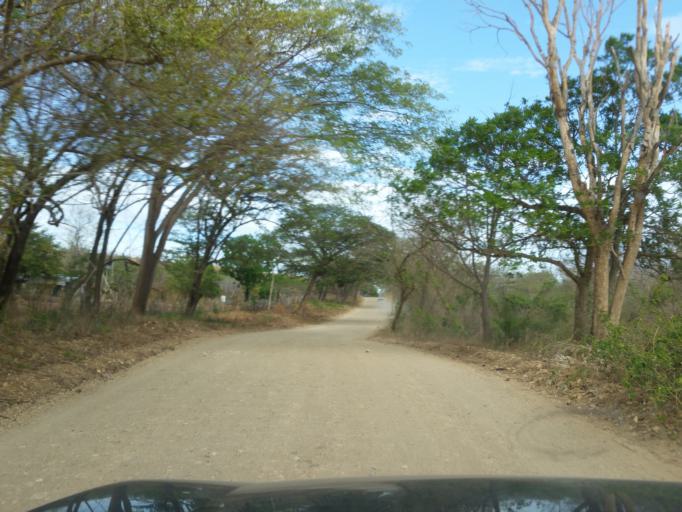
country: NI
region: Rivas
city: Tola
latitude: 11.4050
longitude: -86.0018
